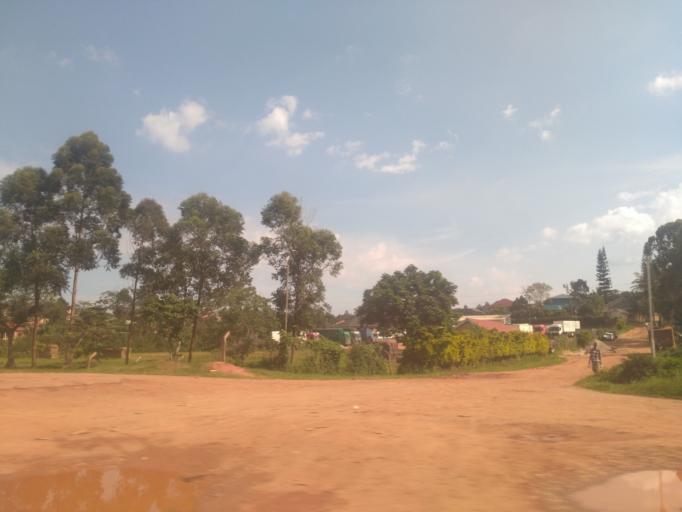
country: UG
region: Central Region
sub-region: Wakiso District
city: Kajansi
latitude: 0.2828
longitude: 32.4853
